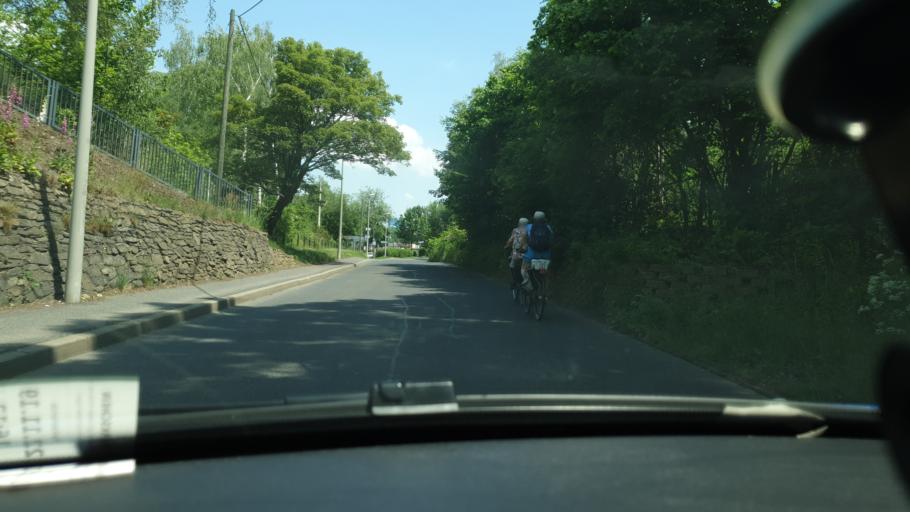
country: DE
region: Saxony
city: Freiberg
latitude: 50.9205
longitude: 13.3576
